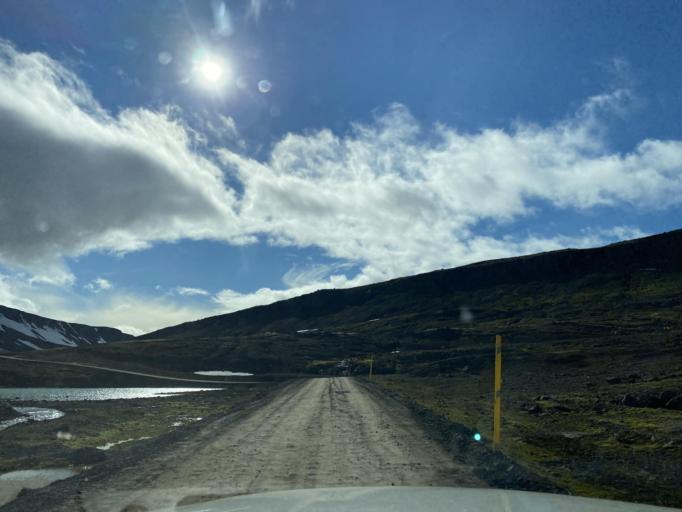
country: IS
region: East
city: Eskifjoerdur
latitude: 65.1678
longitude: -14.1353
